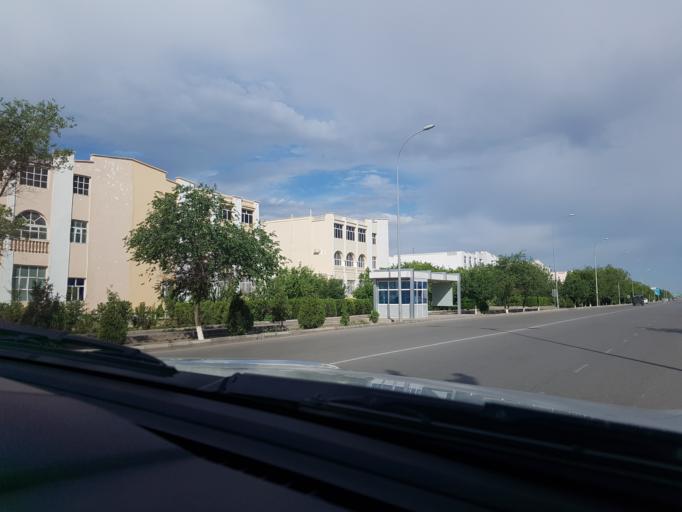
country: TM
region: Dasoguz
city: Dasoguz
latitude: 41.8422
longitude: 59.9389
